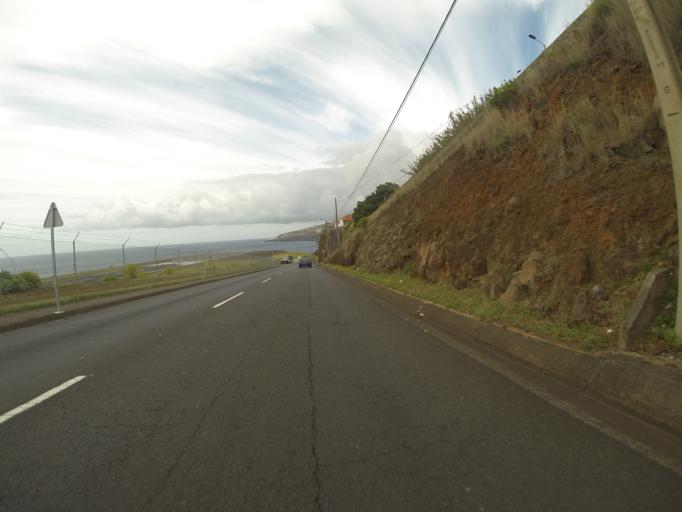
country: PT
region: Madeira
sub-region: Machico
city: Machico
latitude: 32.6924
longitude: -16.7829
